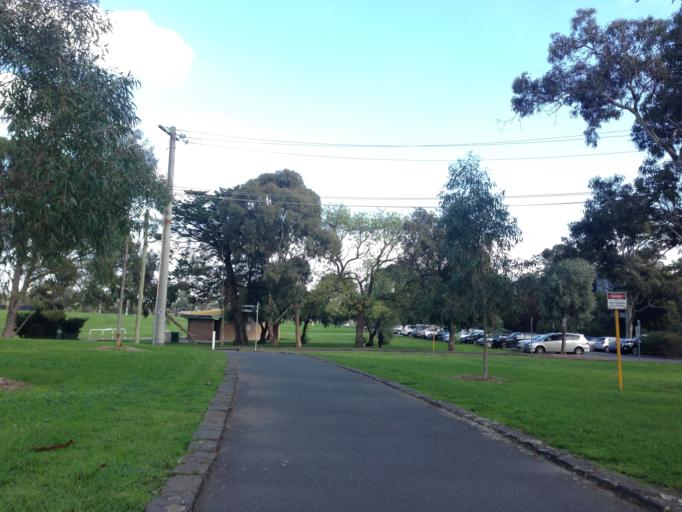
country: AU
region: Victoria
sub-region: Darebin
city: Fairfield
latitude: -37.7848
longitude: 145.0121
